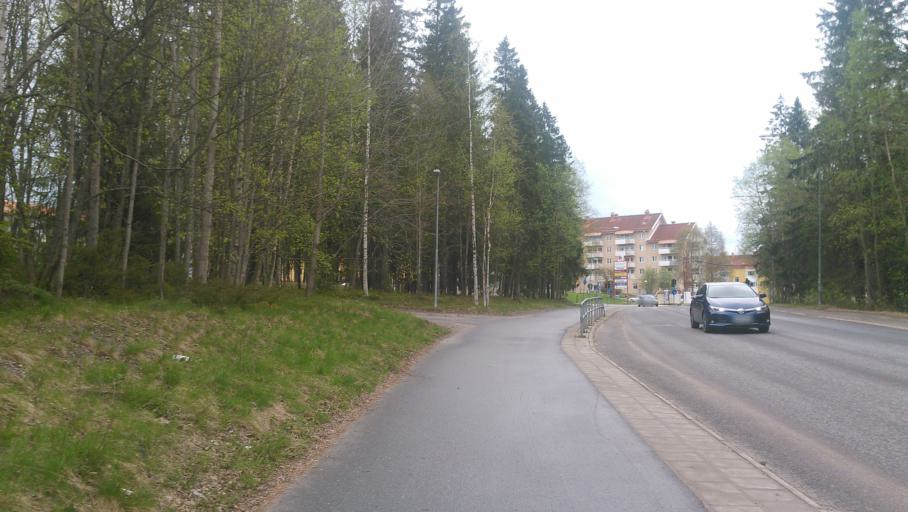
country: SE
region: Vaesterbotten
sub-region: Umea Kommun
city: Umea
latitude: 63.8272
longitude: 20.2923
